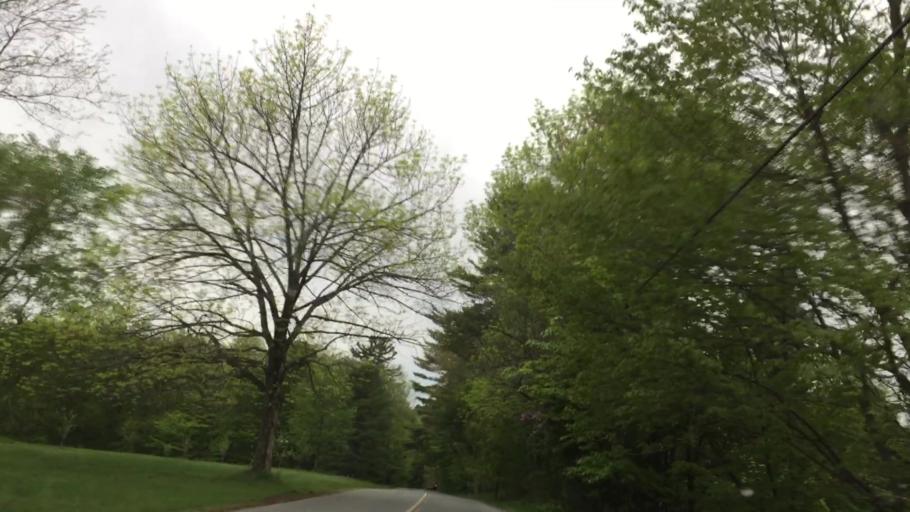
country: US
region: Massachusetts
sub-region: Berkshire County
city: Becket
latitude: 42.2764
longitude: -73.0362
